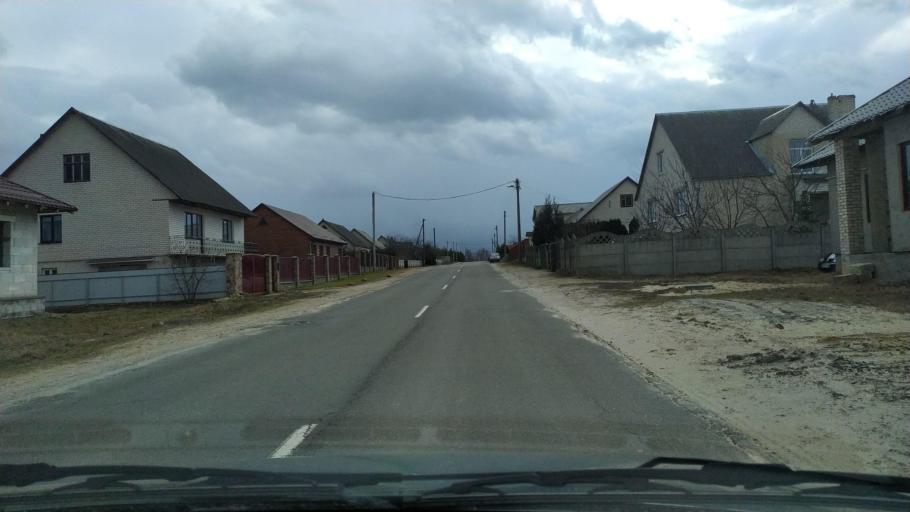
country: BY
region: Brest
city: Kamyanyets
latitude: 52.4000
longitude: 23.8406
